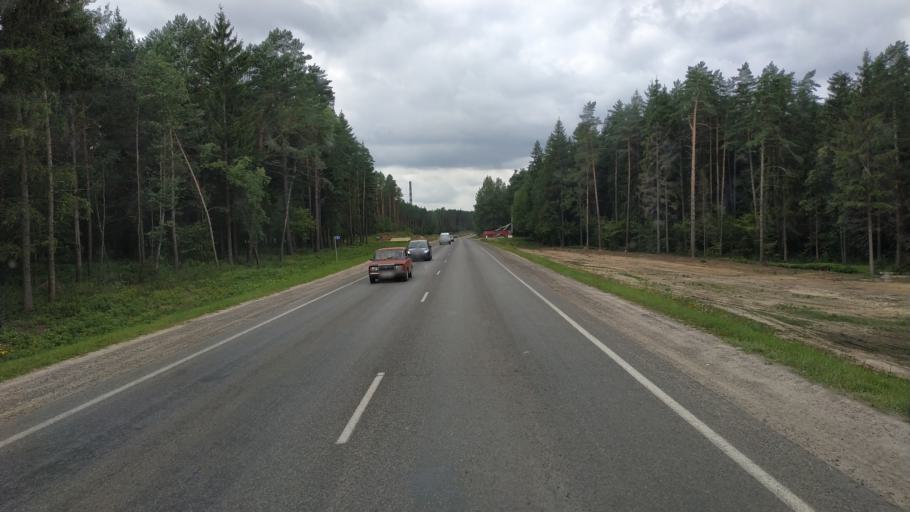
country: BY
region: Mogilev
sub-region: Mahilyowski Rayon
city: Veyno
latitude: 53.8764
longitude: 30.4249
